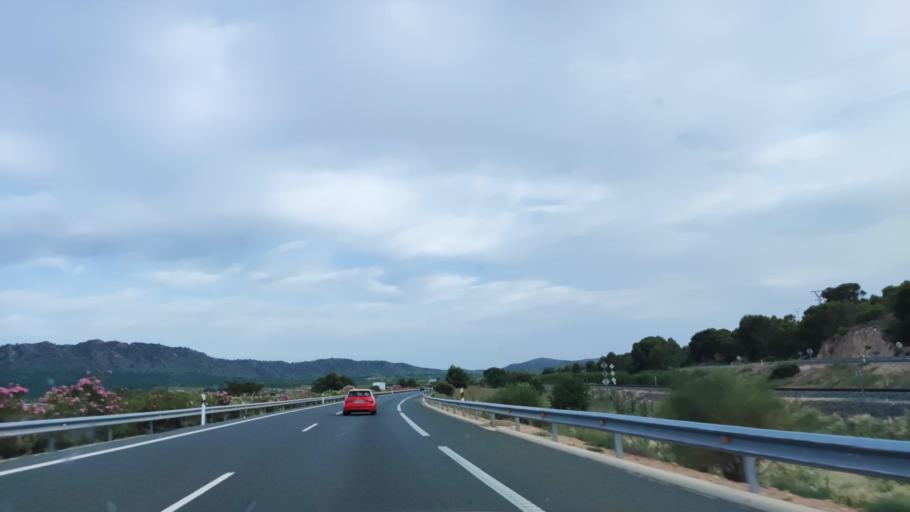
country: ES
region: Castille-La Mancha
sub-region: Provincia de Albacete
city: Tobarra
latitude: 38.6684
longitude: -1.6646
